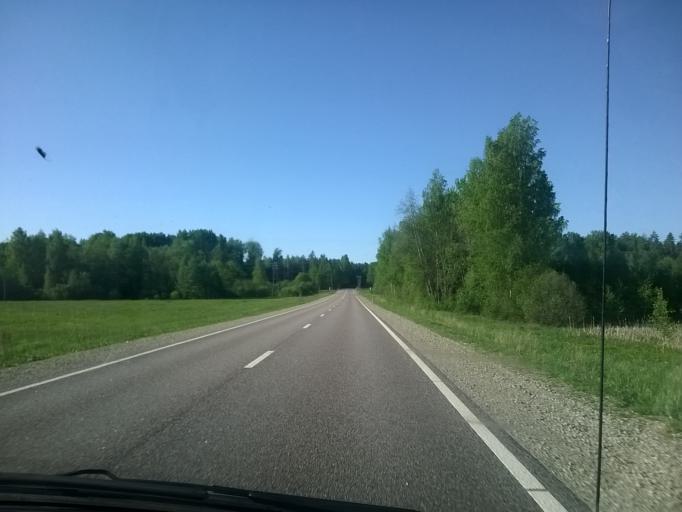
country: LV
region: Valkas Rajons
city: Valka
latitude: 57.7045
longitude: 25.9077
